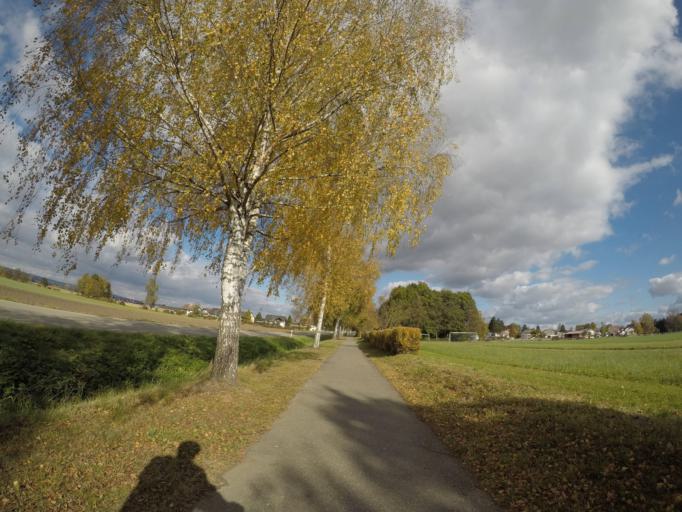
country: DE
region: Baden-Wuerttemberg
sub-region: Tuebingen Region
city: Oberstadion
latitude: 48.1883
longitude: 9.6977
